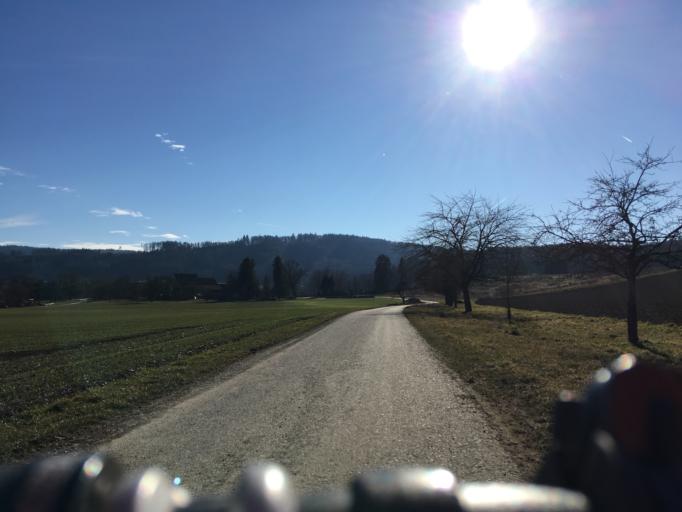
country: CH
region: Schaffhausen
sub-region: Bezirk Stein
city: Ramsen
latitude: 47.6841
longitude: 8.8062
